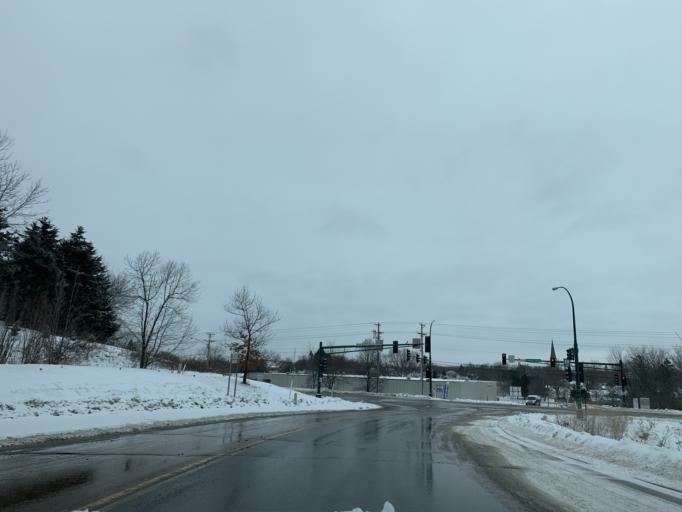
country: US
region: Minnesota
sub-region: Carver County
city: Chaska
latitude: 44.7866
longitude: -93.6091
